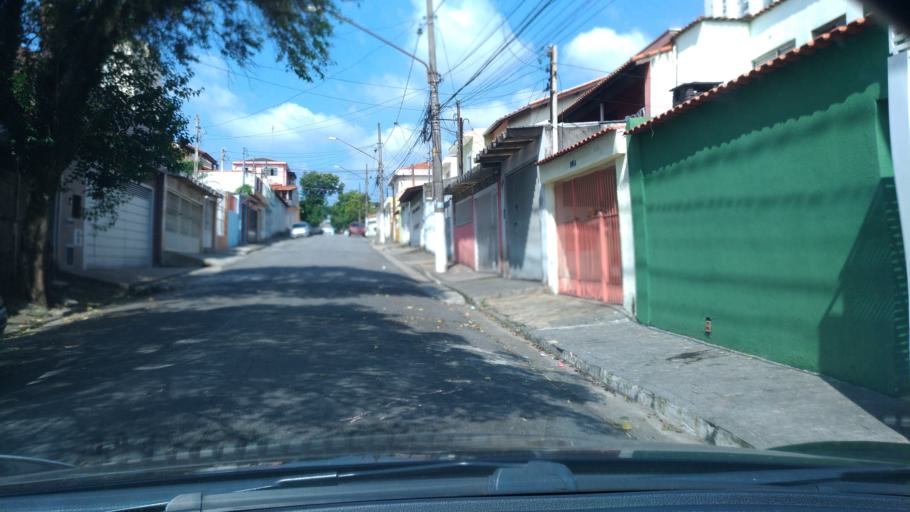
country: BR
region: Sao Paulo
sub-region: Sao Bernardo Do Campo
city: Sao Bernardo do Campo
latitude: -23.6968
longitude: -46.5793
